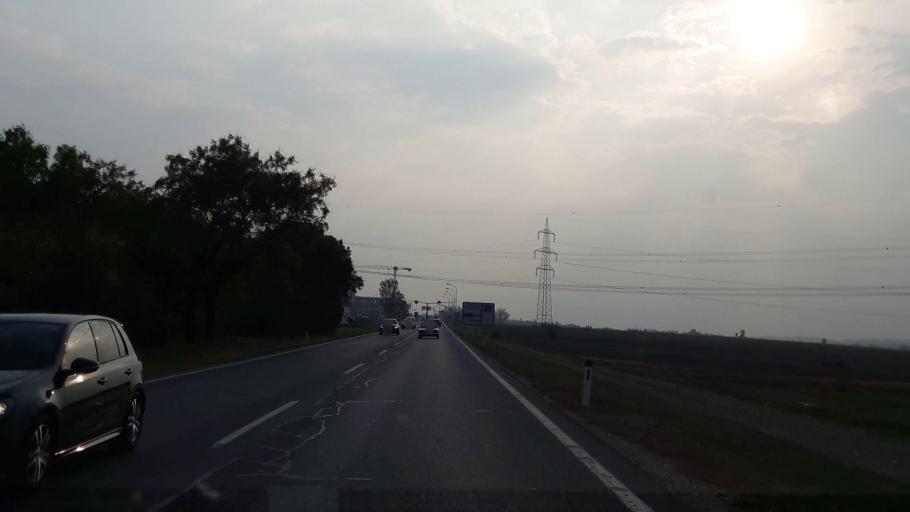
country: AT
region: Burgenland
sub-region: Politischer Bezirk Neusiedl am See
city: Parndorf
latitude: 47.9870
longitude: 16.8532
